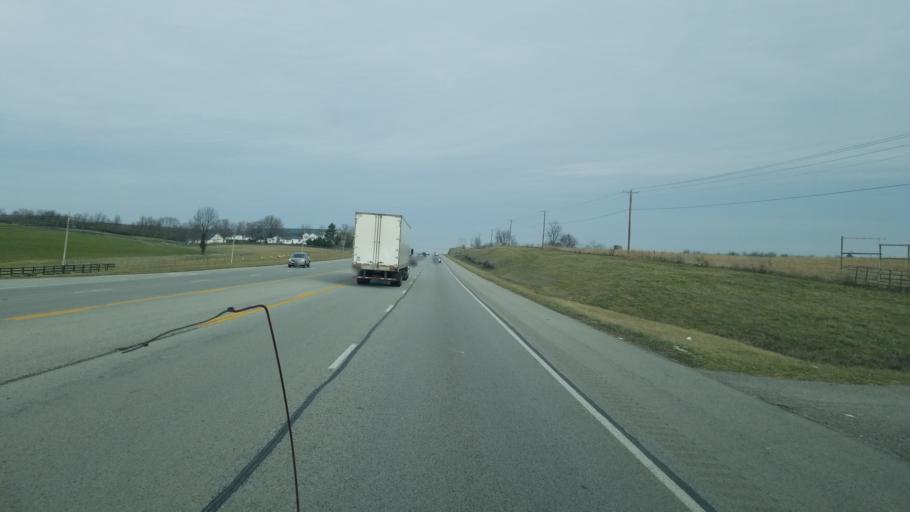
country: US
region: Kentucky
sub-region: Boyle County
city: Junction City
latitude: 37.6052
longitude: -84.7738
